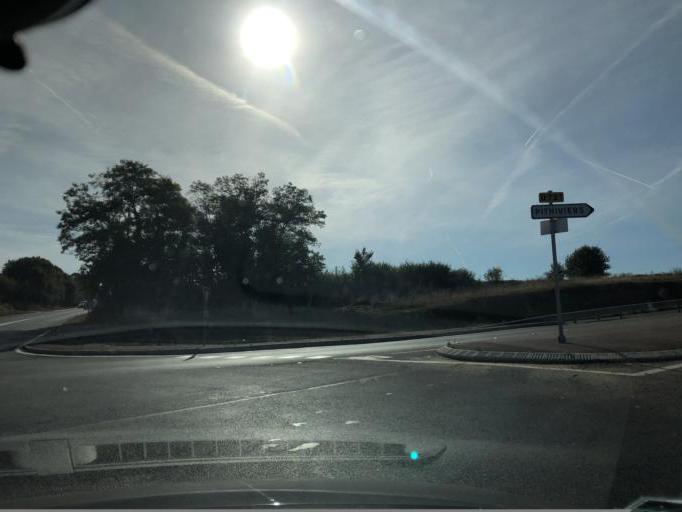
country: FR
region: Ile-de-France
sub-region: Departement de l'Essonne
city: Morigny-Champigny
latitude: 48.4225
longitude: 2.1790
